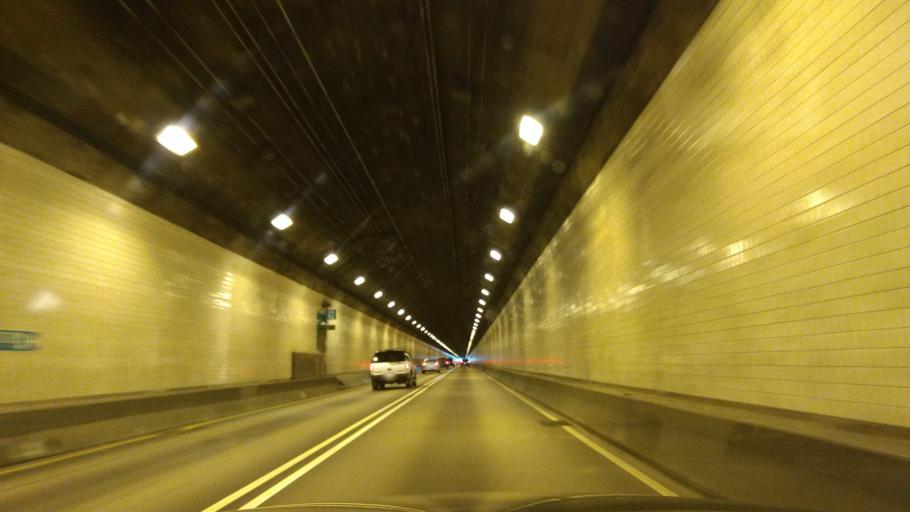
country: US
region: Pennsylvania
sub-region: Allegheny County
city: Homestead
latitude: 40.4267
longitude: -79.9167
